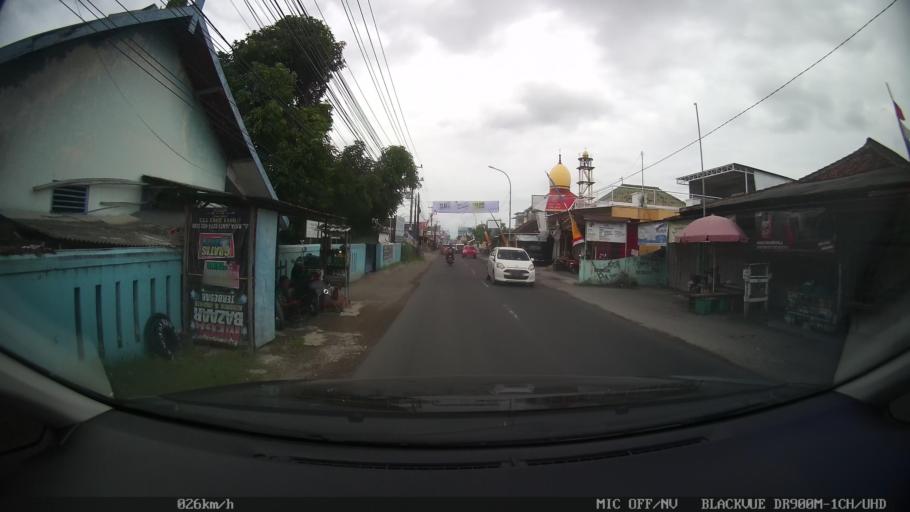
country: ID
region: Daerah Istimewa Yogyakarta
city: Yogyakarta
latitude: -7.8289
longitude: 110.4107
